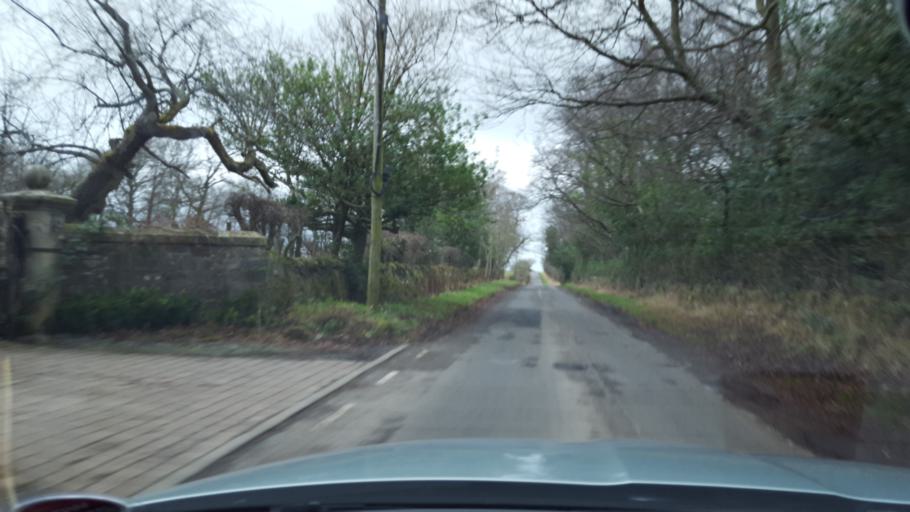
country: GB
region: Scotland
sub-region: West Lothian
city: Kirknewton
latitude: 55.8613
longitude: -3.4280
